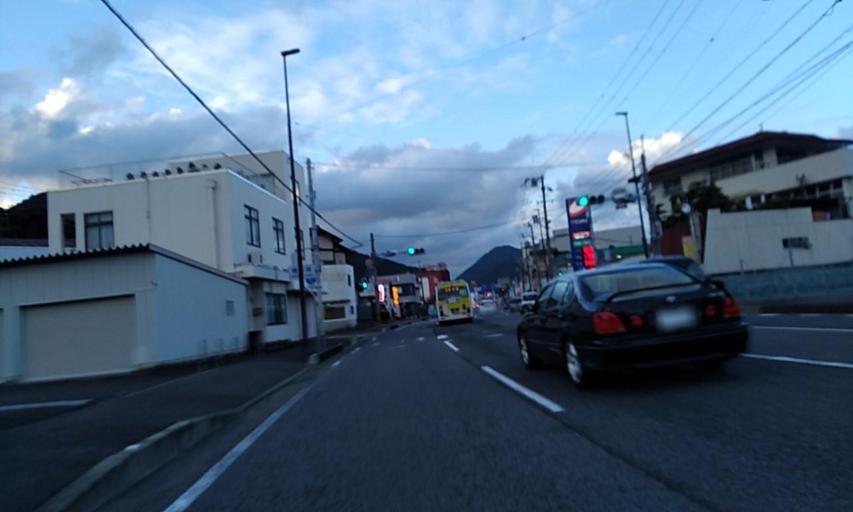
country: JP
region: Wakayama
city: Shingu
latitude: 33.7169
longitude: 135.9874
